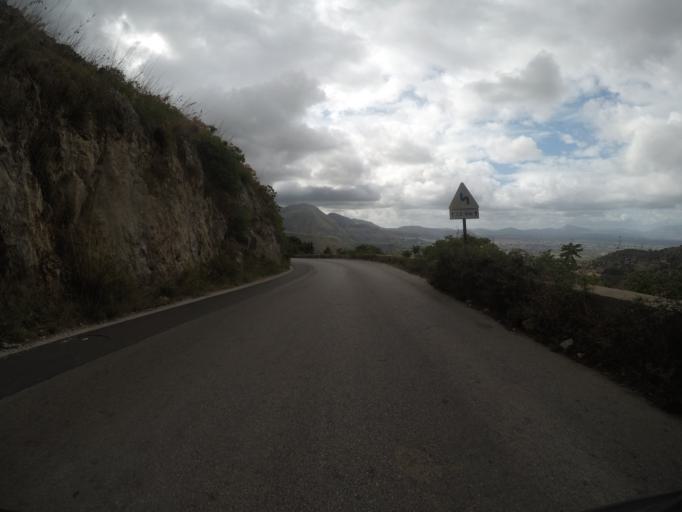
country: IT
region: Sicily
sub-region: Palermo
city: Montelepre
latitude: 38.0964
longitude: 13.1672
